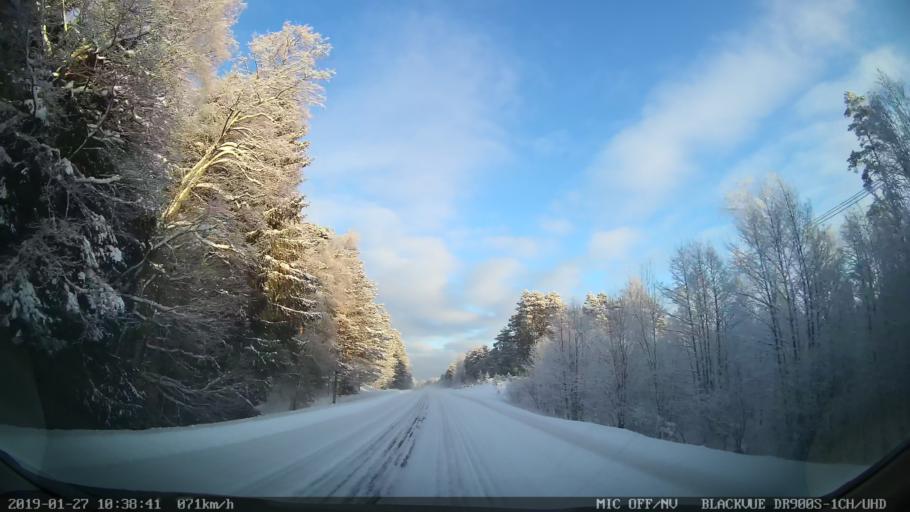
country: EE
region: Harju
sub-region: Raasiku vald
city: Raasiku
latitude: 59.4838
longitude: 25.2597
